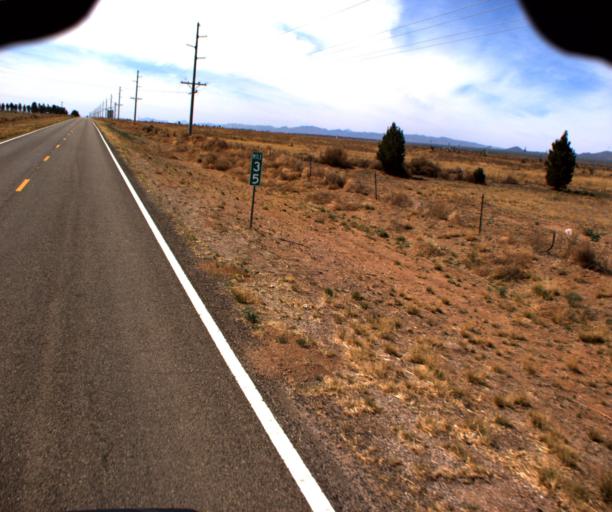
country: US
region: Arizona
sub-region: Cochise County
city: Tombstone
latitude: 31.8400
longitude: -109.6952
